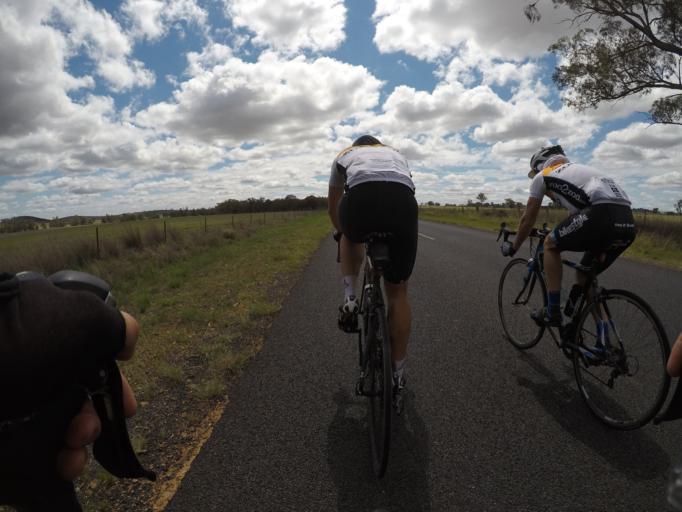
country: AU
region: New South Wales
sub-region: Dubbo Municipality
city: Dubbo
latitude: -32.4798
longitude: 148.5608
